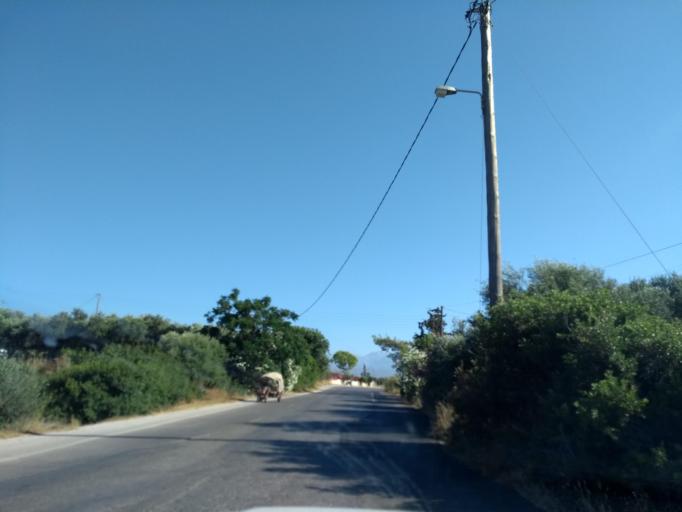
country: GR
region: Crete
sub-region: Nomos Chanias
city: Pithari
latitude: 35.5722
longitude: 24.0916
